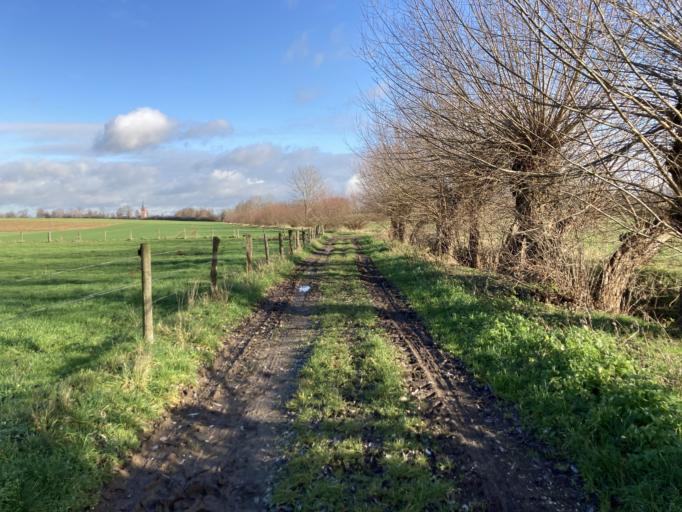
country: DE
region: North Rhine-Westphalia
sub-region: Regierungsbezirk Koln
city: Titz
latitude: 50.9834
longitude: 6.3727
